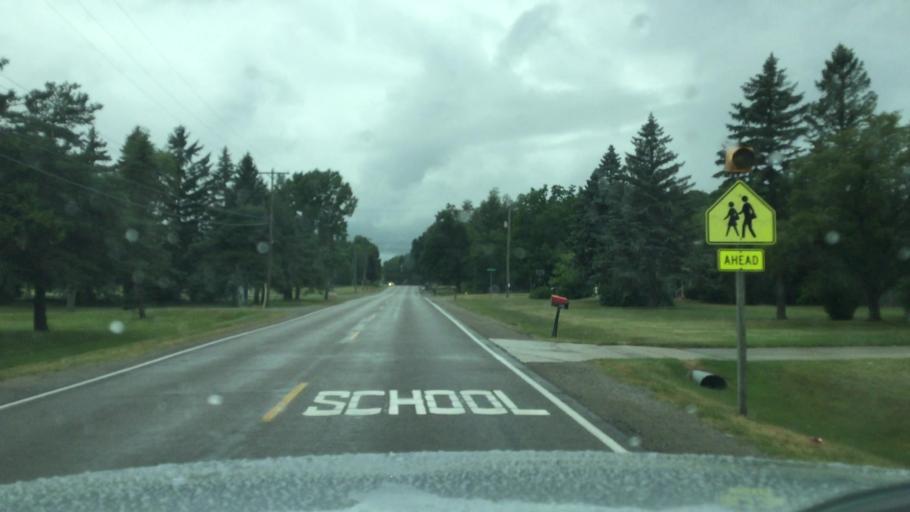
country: US
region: Michigan
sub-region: Genesee County
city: Beecher
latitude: 43.0753
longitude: -83.7395
